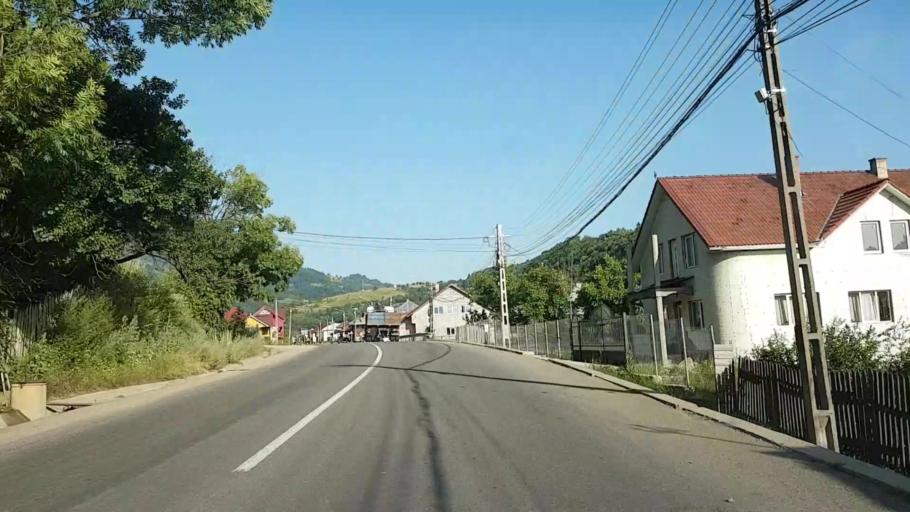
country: RO
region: Bistrita-Nasaud
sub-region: Comuna Tiha Bargaului
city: Tureac
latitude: 47.2156
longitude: 24.8445
